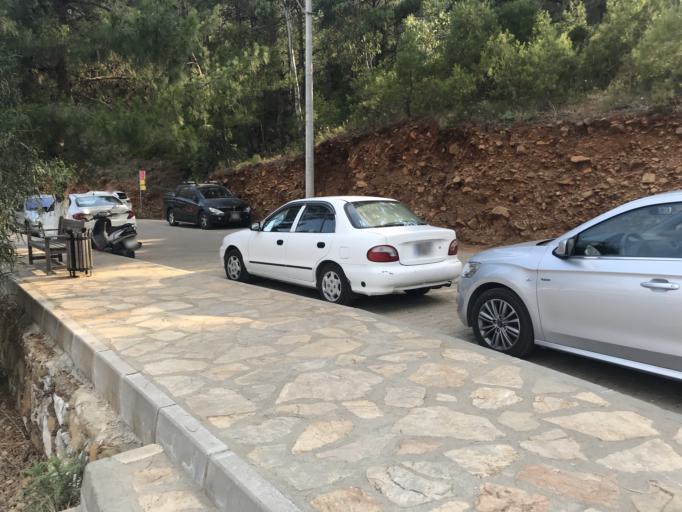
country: TR
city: Dalyan
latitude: 36.8288
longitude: 28.5482
